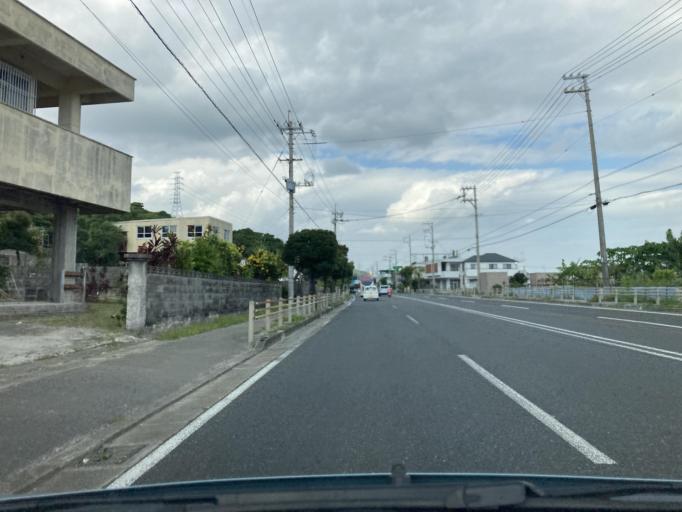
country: JP
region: Okinawa
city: Ginowan
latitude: 26.2456
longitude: 127.7814
